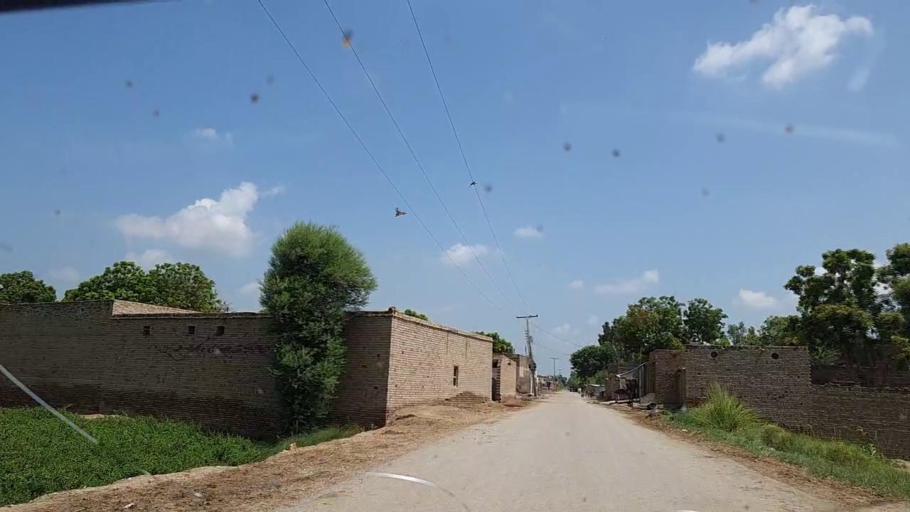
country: PK
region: Sindh
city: Tharu Shah
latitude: 26.9602
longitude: 68.1003
